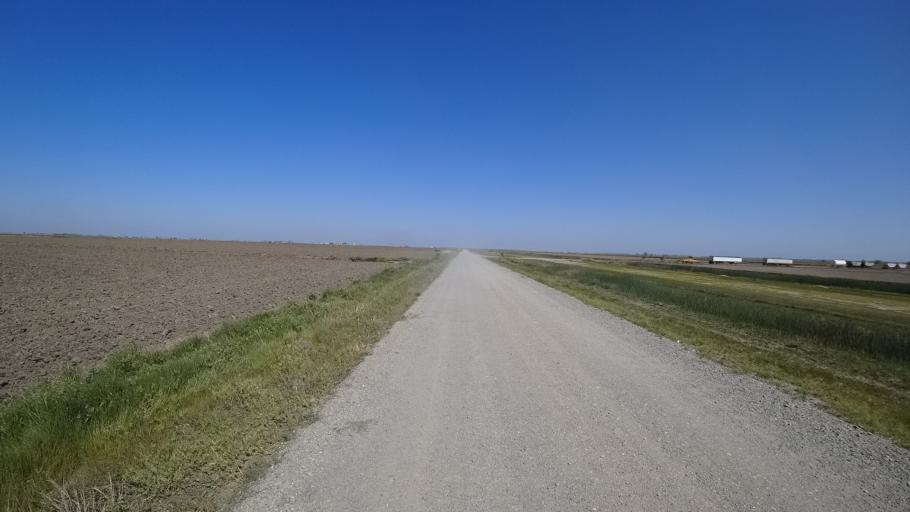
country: US
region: California
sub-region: Glenn County
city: Willows
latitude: 39.4845
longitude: -122.0560
